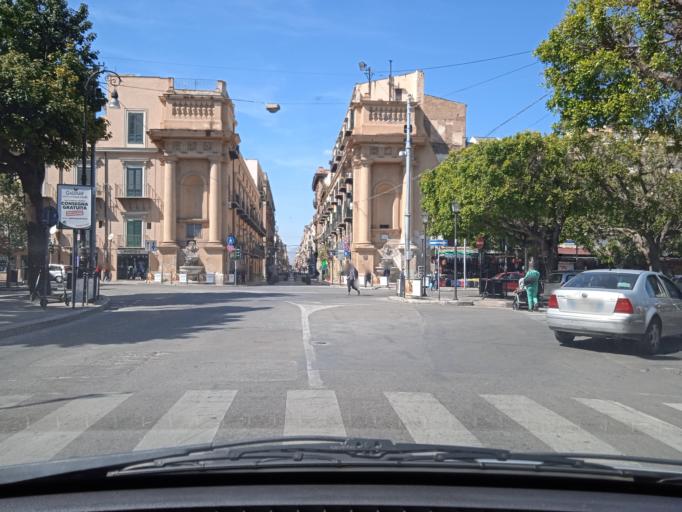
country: IT
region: Sicily
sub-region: Palermo
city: Palermo
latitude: 38.1097
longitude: 13.3652
